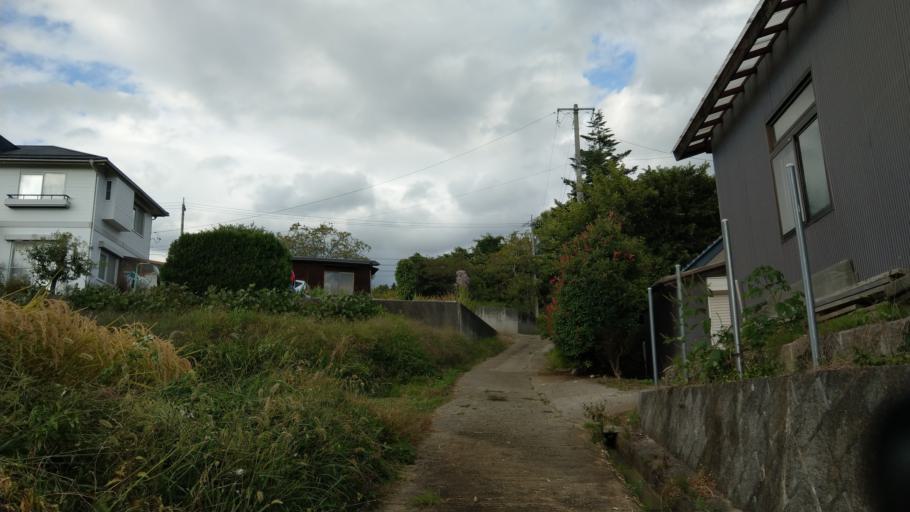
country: JP
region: Nagano
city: Komoro
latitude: 36.3501
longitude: 138.4177
